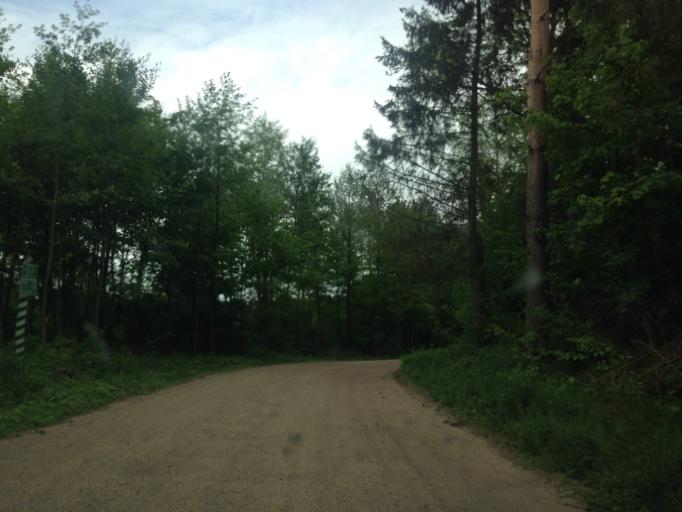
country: PL
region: Kujawsko-Pomorskie
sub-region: Powiat brodnicki
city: Bartniczka
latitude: 53.2747
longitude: 19.5761
